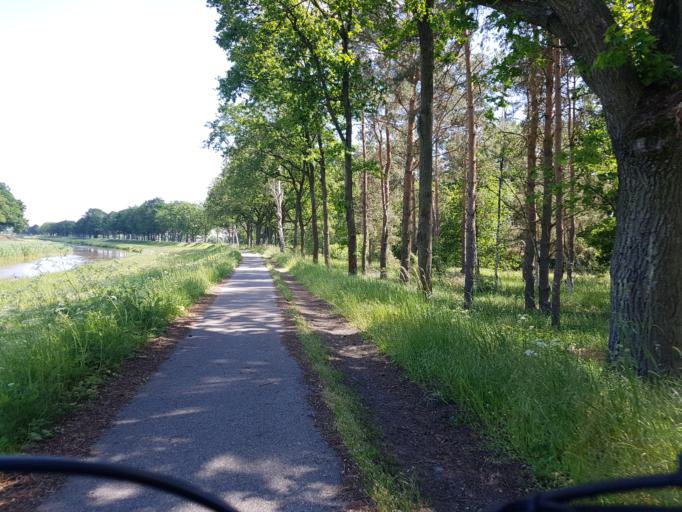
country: DE
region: Brandenburg
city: Bad Liebenwerda
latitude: 51.4836
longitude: 13.4376
